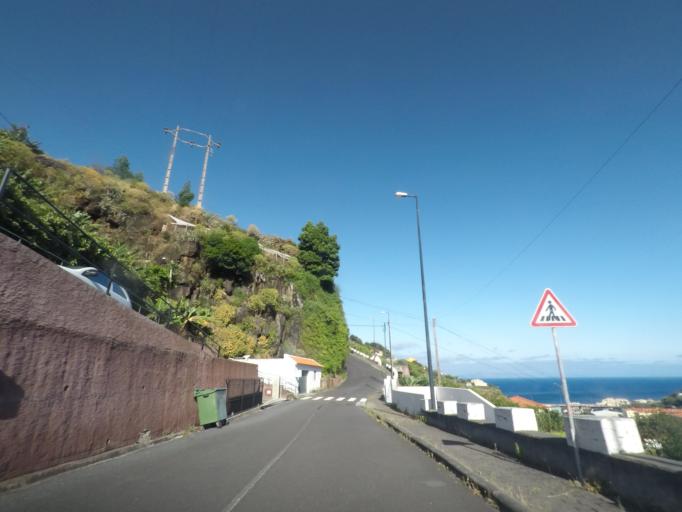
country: PT
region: Madeira
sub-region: Santa Cruz
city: Santa Cruz
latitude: 32.6927
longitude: -16.7996
